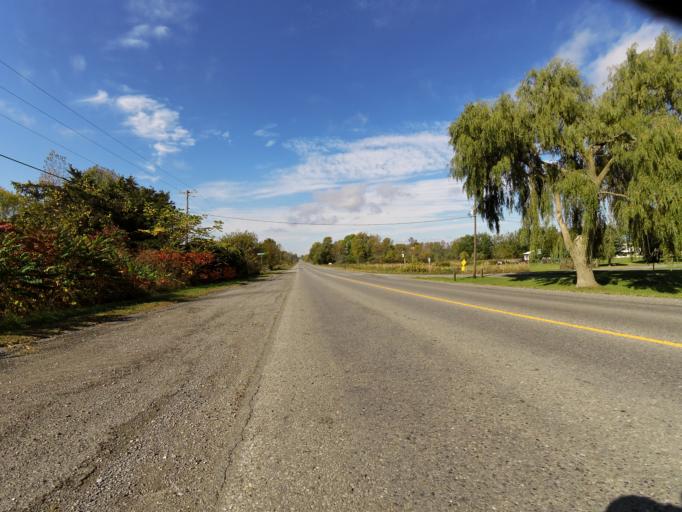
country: CA
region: Ontario
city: Prince Edward
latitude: 43.9980
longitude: -77.1959
